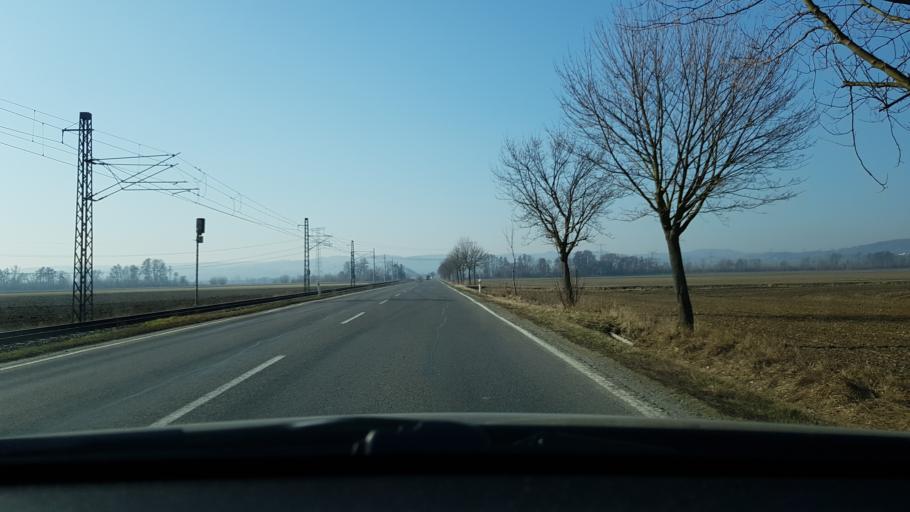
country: CZ
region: Olomoucky
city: Postrelmov
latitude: 49.9006
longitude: 16.9087
